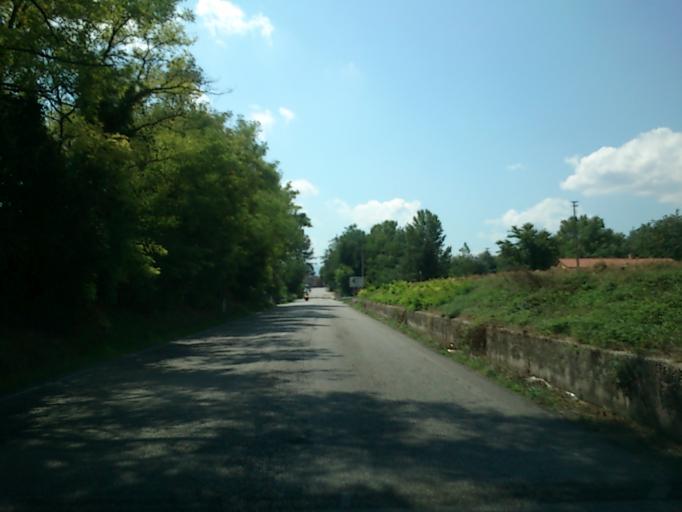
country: IT
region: The Marches
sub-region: Provincia di Pesaro e Urbino
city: Calcinelli
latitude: 43.7446
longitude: 12.9106
